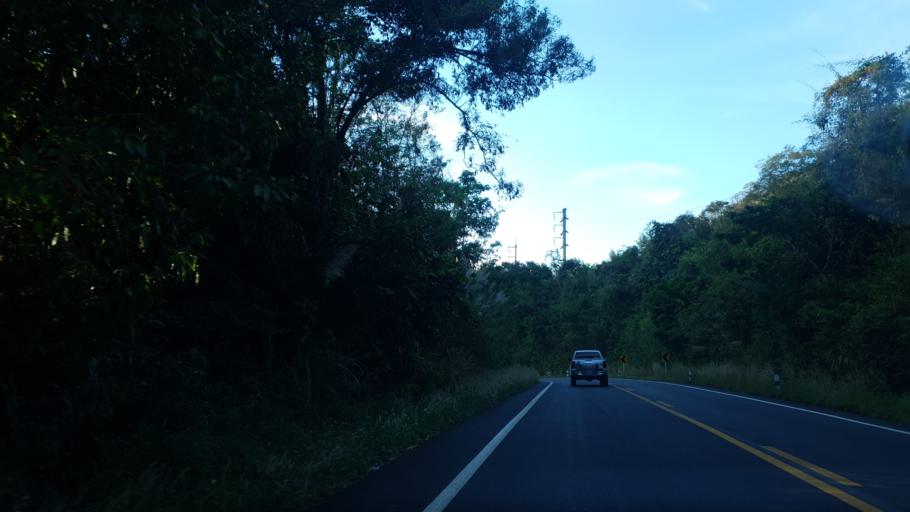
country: TH
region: Loei
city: Dan Sai
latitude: 17.2289
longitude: 101.0579
